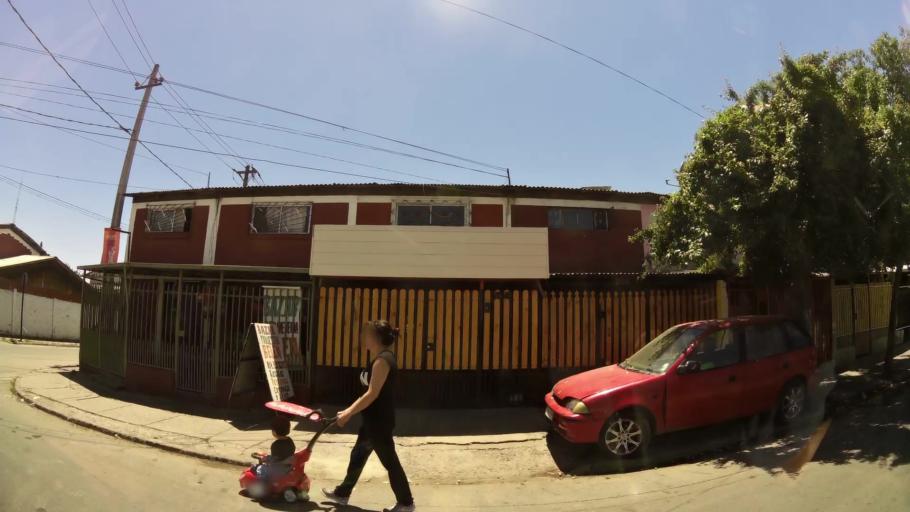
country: CL
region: Santiago Metropolitan
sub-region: Provincia de Santiago
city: La Pintana
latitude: -33.5810
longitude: -70.6675
